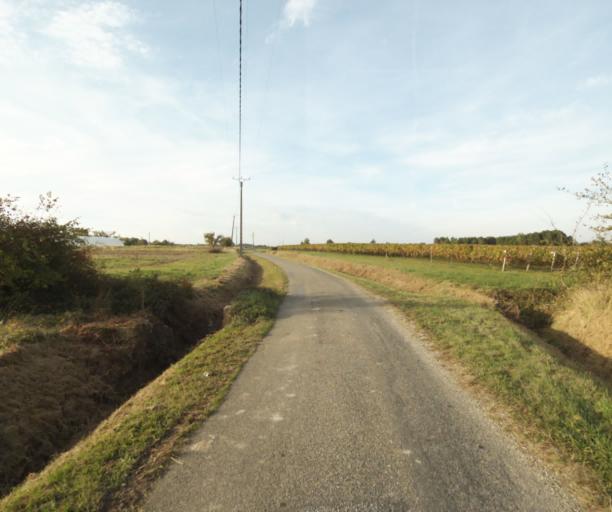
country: FR
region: Midi-Pyrenees
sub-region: Departement du Tarn-et-Garonne
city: Campsas
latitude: 43.8796
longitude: 1.3484
